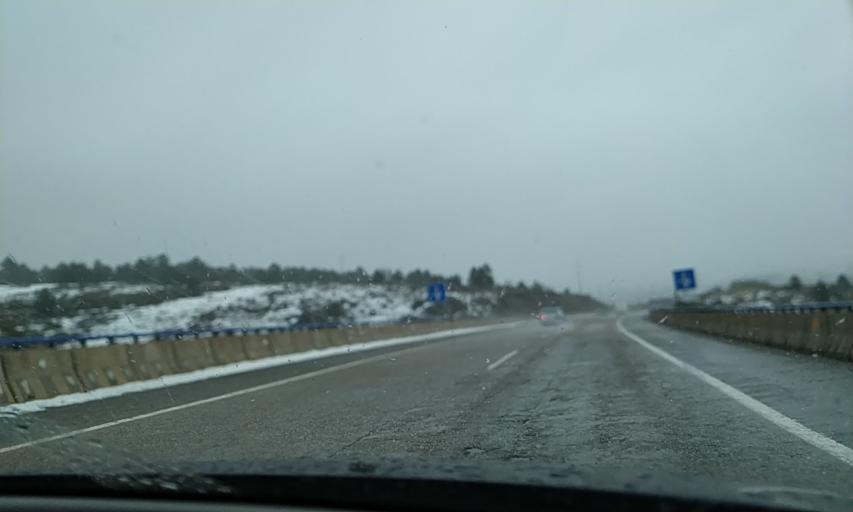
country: ES
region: Castille and Leon
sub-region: Provincia de Zamora
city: Requejo
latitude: 42.0345
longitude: -6.7584
